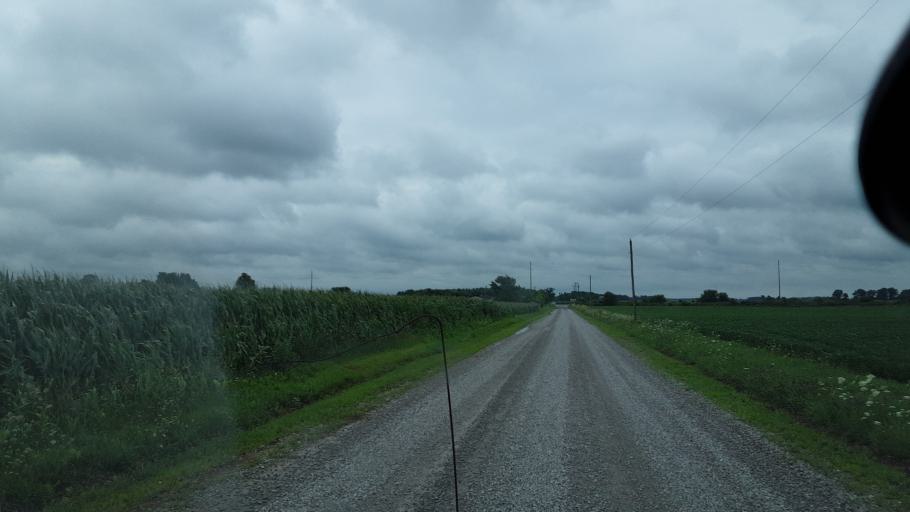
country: US
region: Indiana
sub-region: Wells County
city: Ossian
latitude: 40.8355
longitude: -85.0724
